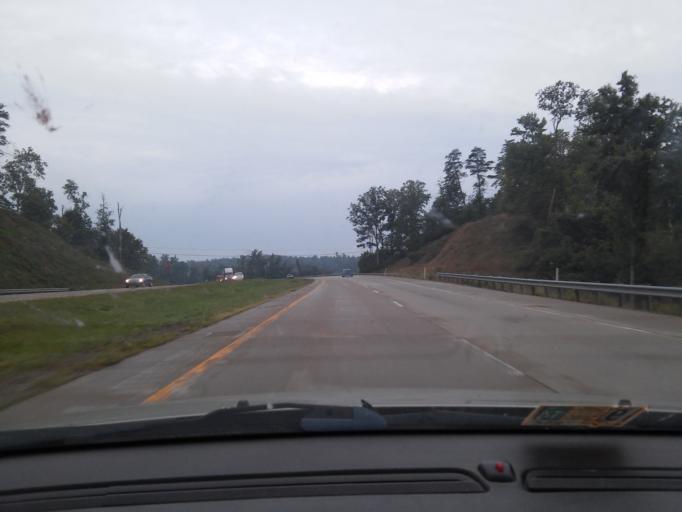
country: US
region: West Virginia
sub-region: Putnam County
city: Teays Valley
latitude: 38.4911
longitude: -81.9343
